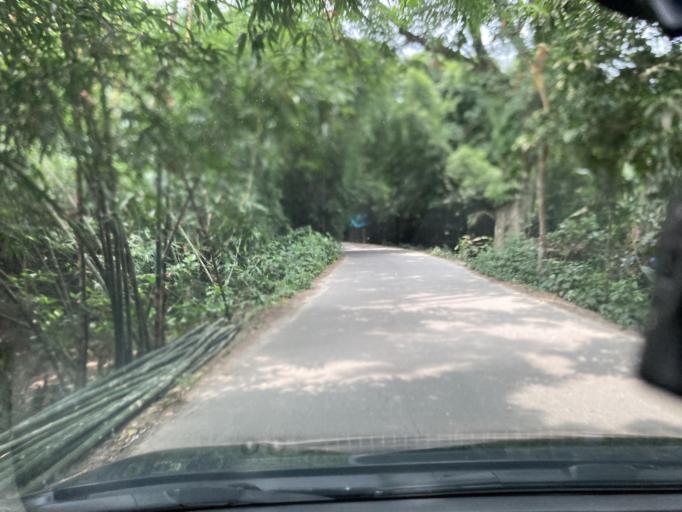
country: BD
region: Dhaka
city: Dohar
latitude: 23.8113
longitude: 90.0461
